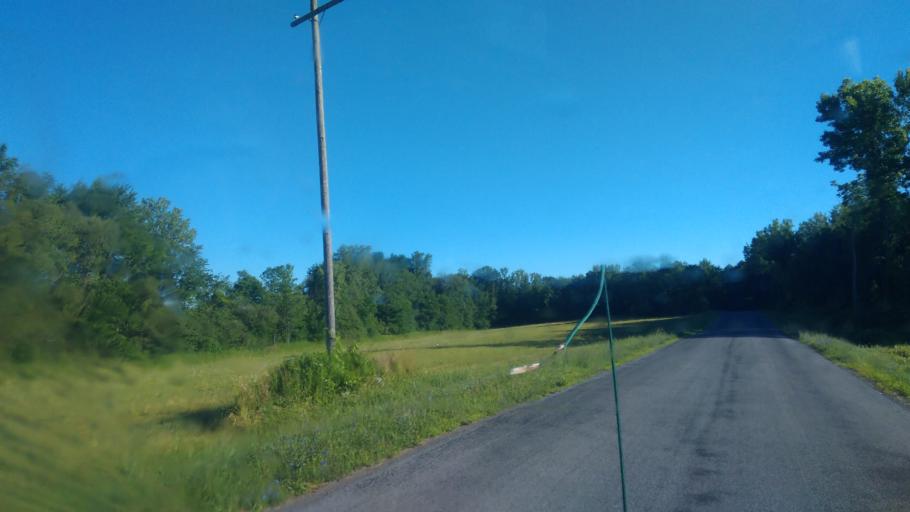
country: US
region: New York
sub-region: Wayne County
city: Lyons
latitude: 43.1320
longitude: -77.0380
